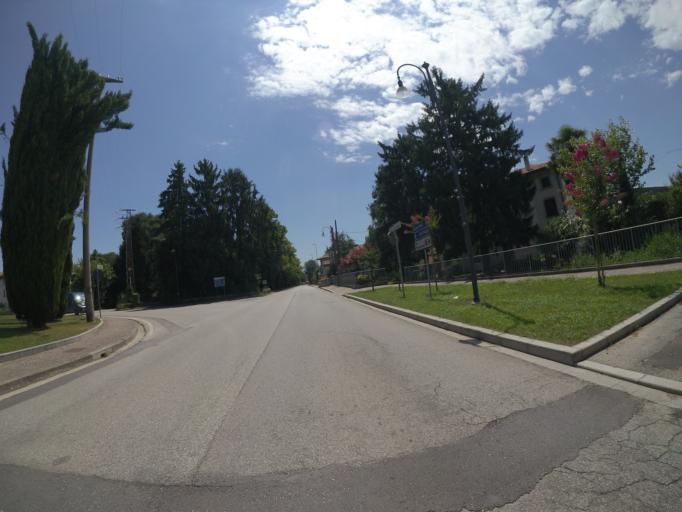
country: IT
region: Friuli Venezia Giulia
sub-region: Provincia di Udine
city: Lestizza
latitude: 45.9759
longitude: 13.1393
